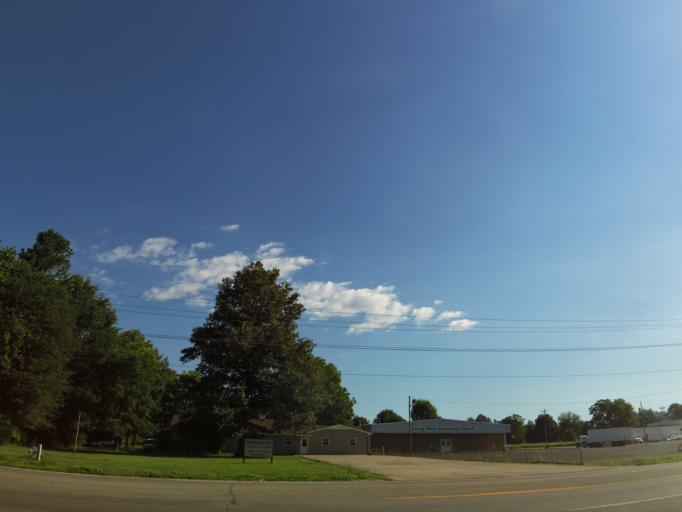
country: US
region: Arkansas
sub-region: Clay County
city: Corning
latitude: 36.4113
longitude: -90.5940
